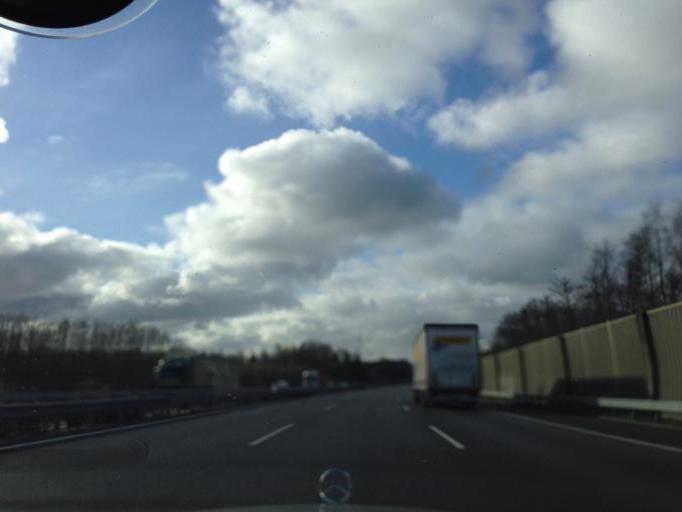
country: DE
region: Lower Saxony
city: Marxen
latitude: 53.3650
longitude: 10.0350
